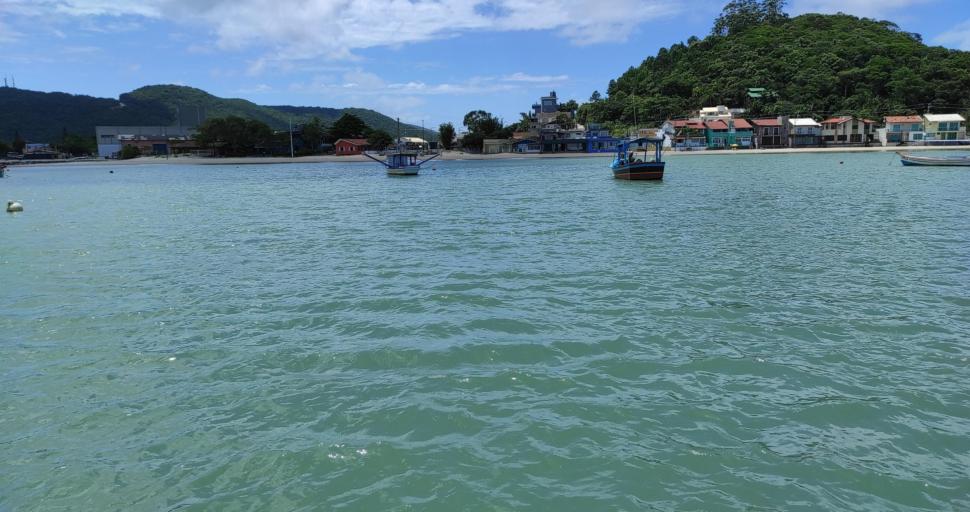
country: BR
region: Santa Catarina
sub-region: Porto Belo
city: Porto Belo
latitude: -27.1828
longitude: -48.5239
